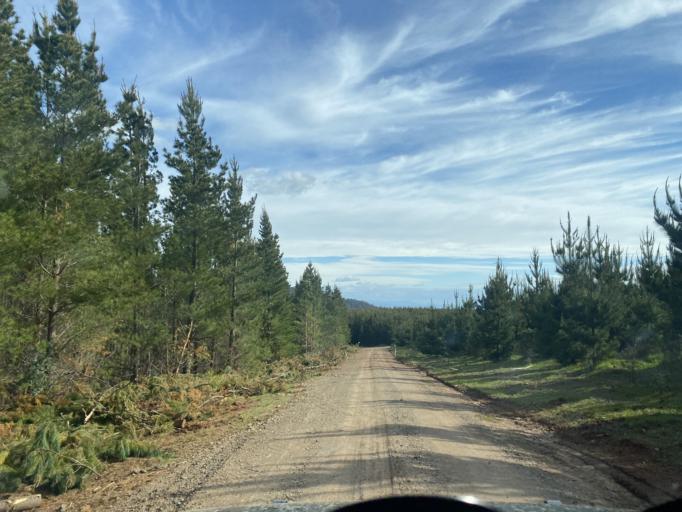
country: AU
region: Victoria
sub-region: Mansfield
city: Mansfield
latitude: -36.8341
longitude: 146.1792
